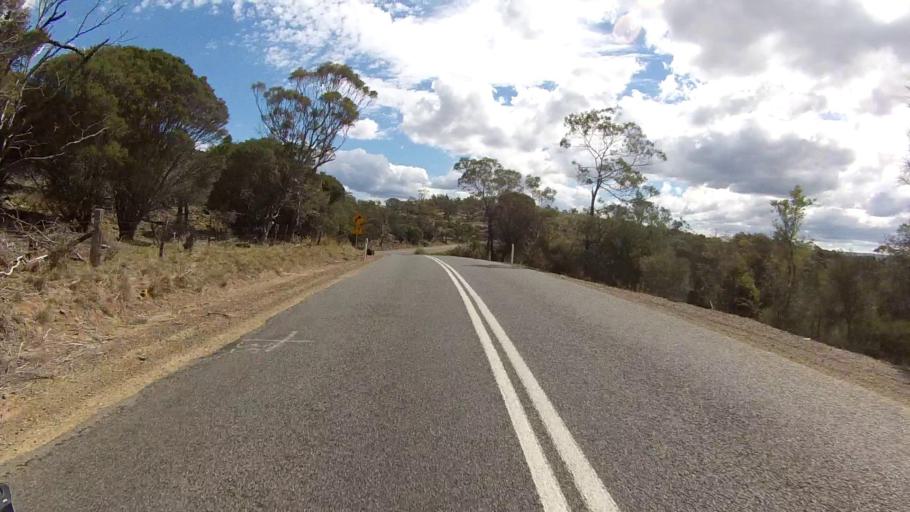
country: AU
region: Tasmania
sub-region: Break O'Day
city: St Helens
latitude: -41.9940
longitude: 148.1086
